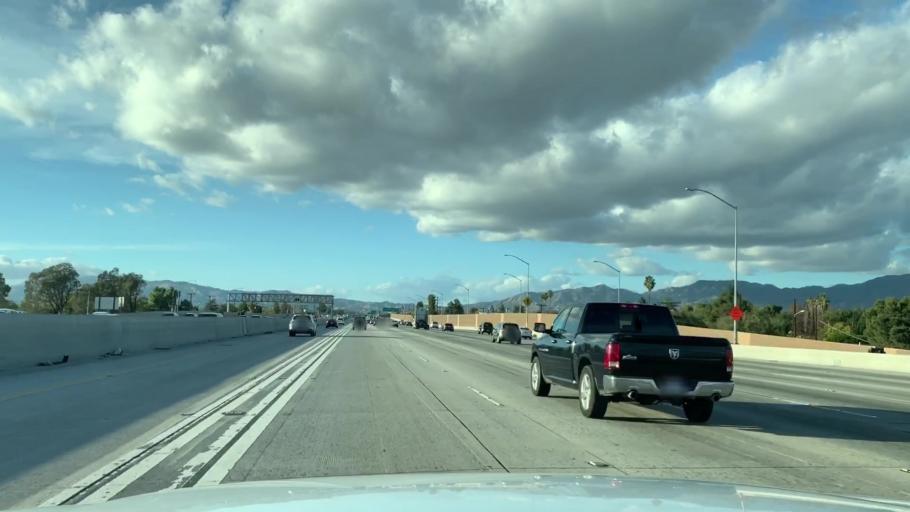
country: US
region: California
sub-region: Los Angeles County
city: San Fernando
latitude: 34.2450
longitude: -118.4226
